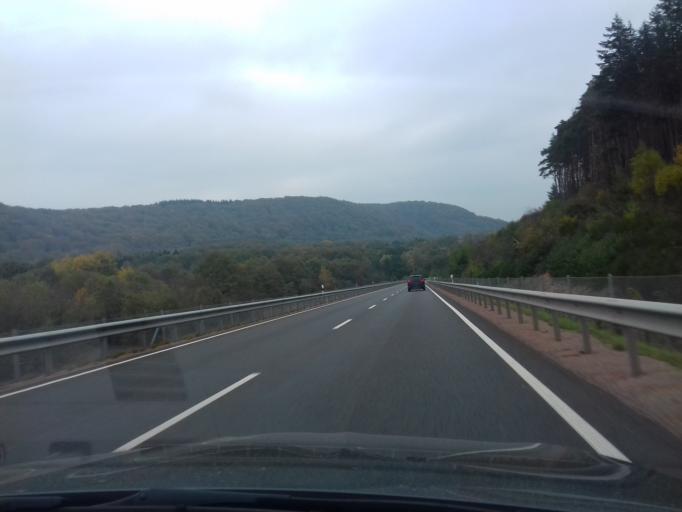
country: DE
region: Rheinland-Pfalz
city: Tawern
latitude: 49.6794
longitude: 6.5400
